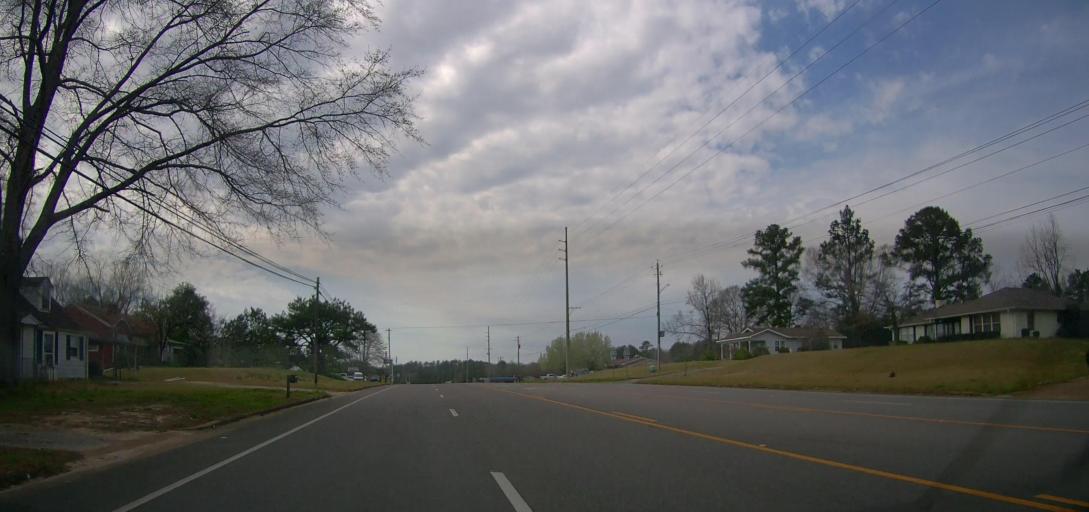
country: US
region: Alabama
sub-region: Marion County
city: Winfield
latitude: 33.9310
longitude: -87.7799
